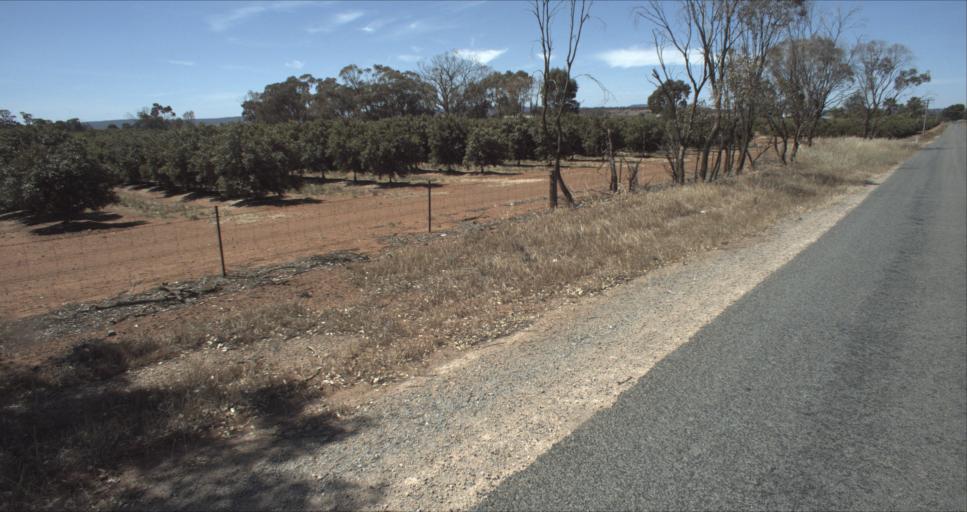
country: AU
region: New South Wales
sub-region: Leeton
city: Leeton
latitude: -34.5905
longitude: 146.4576
